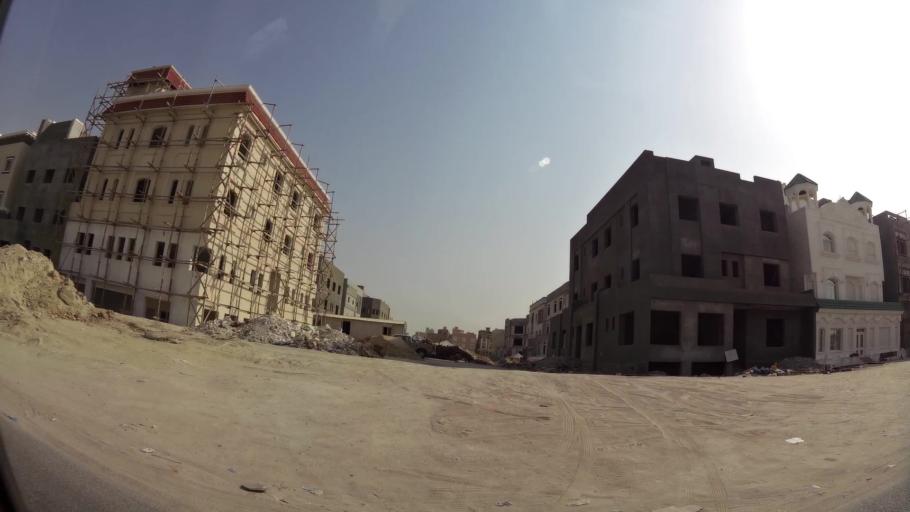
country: KW
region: Muhafazat al Jahra'
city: Al Jahra'
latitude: 29.3512
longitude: 47.7449
